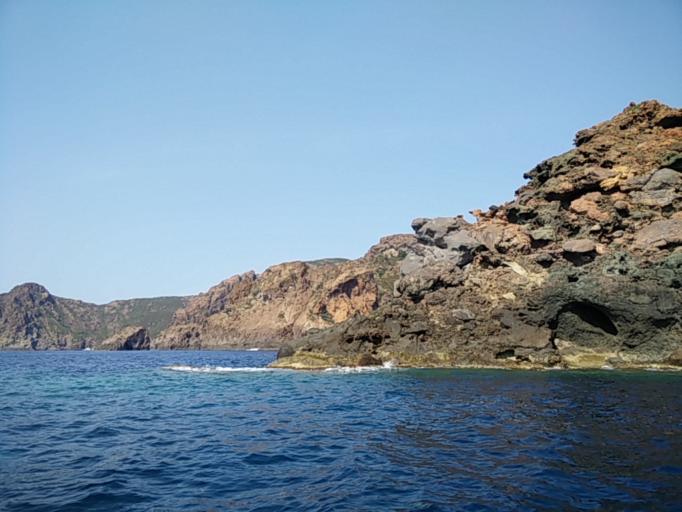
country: FR
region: Corsica
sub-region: Departement de la Corse-du-Sud
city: Cargese
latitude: 42.3494
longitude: 8.5518
